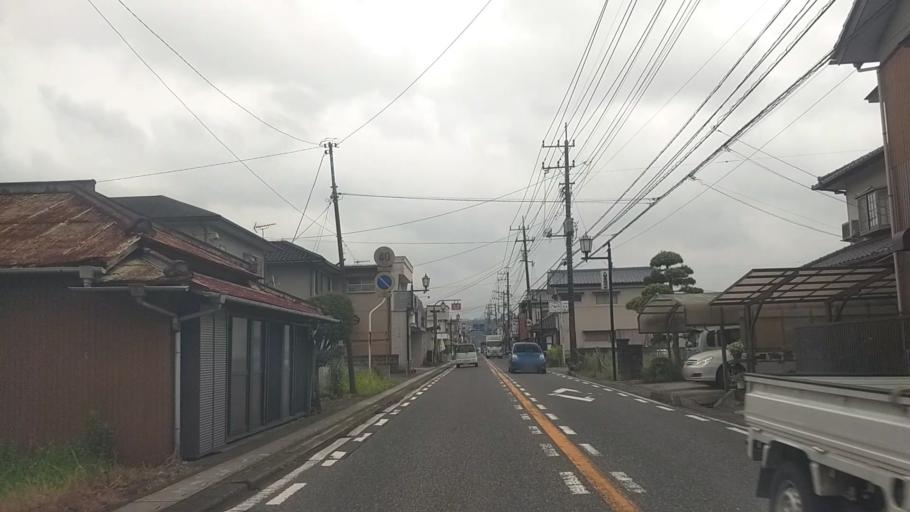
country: JP
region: Chiba
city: Kisarazu
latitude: 35.2975
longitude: 140.0760
